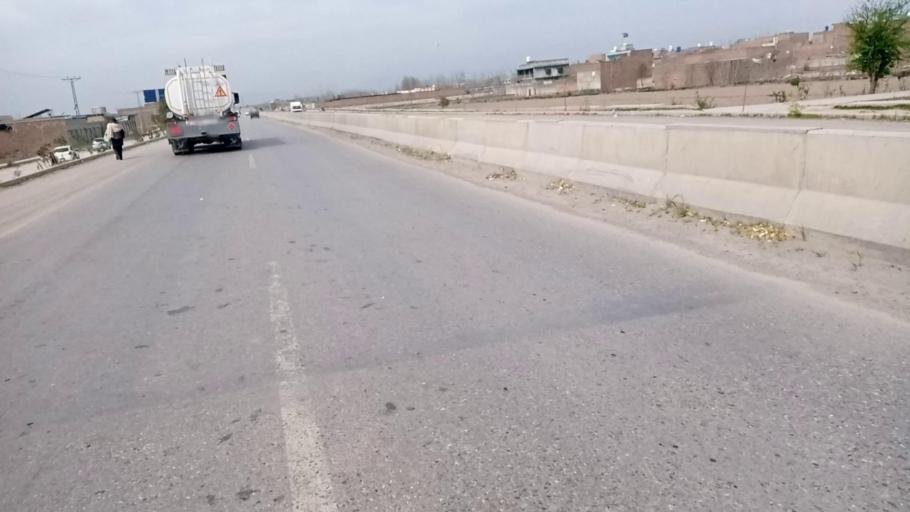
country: PK
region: Khyber Pakhtunkhwa
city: Peshawar
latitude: 34.0408
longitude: 71.6184
